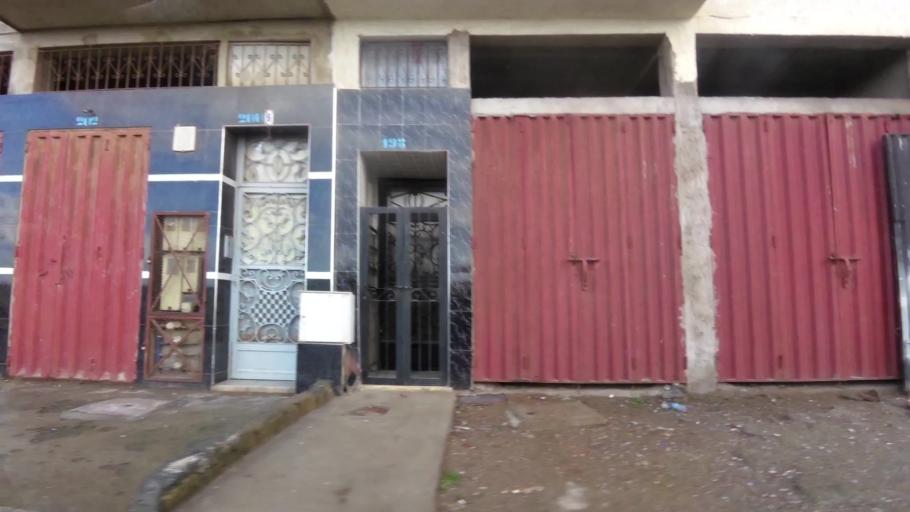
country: MA
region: Grand Casablanca
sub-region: Nouaceur
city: Bouskoura
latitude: 33.5372
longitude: -7.7048
